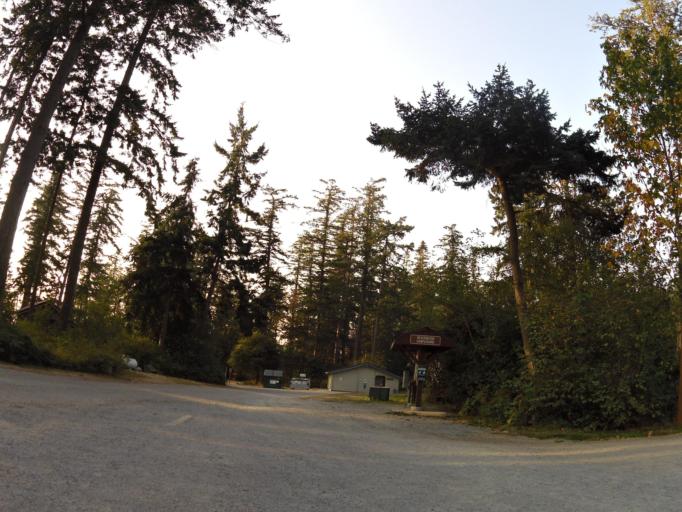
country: US
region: Washington
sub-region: Skagit County
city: Anacortes
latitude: 48.4886
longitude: -122.4793
